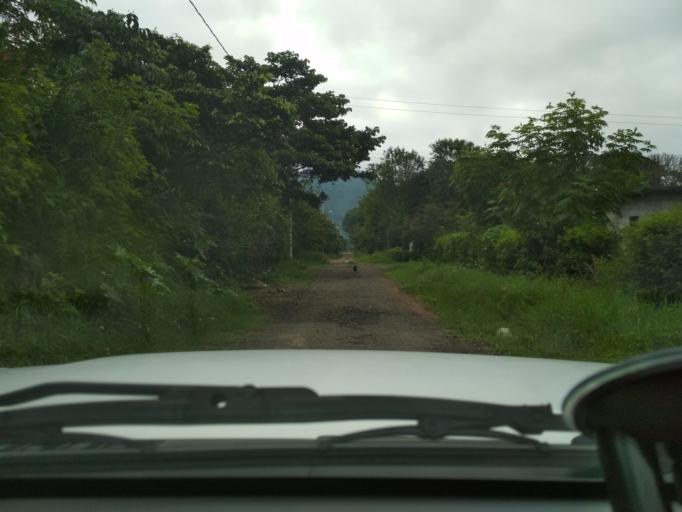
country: MX
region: Veracruz
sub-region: Ixtaczoquitlan
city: Buenavista
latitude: 18.9154
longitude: -97.0498
